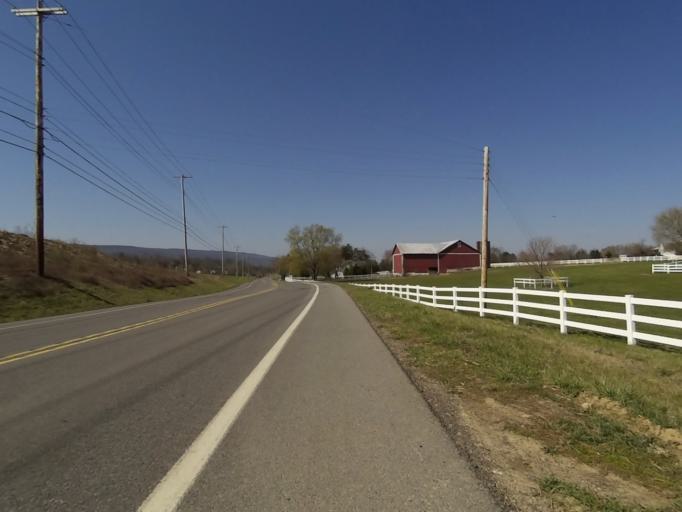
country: US
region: Pennsylvania
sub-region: Centre County
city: Pine Grove Mills
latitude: 40.7325
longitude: -77.9276
